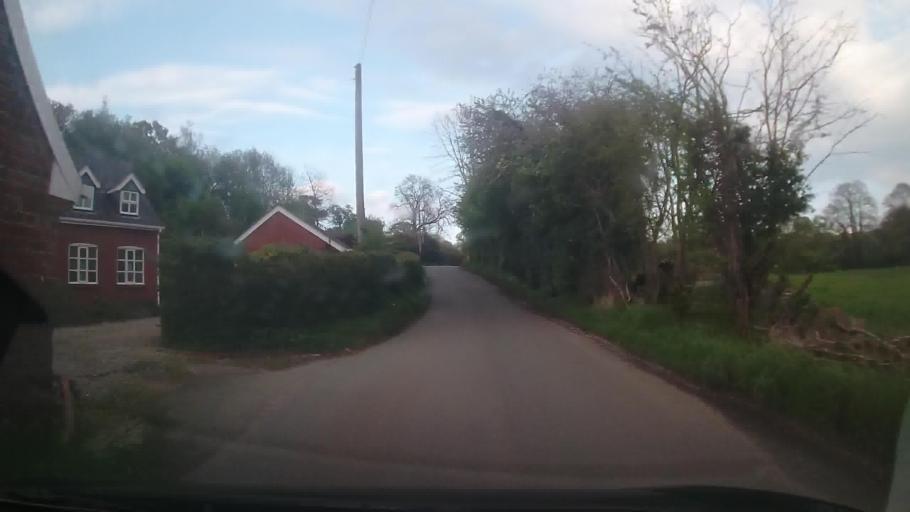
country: GB
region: England
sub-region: Shropshire
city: Ellesmere
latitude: 52.9455
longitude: -2.8711
